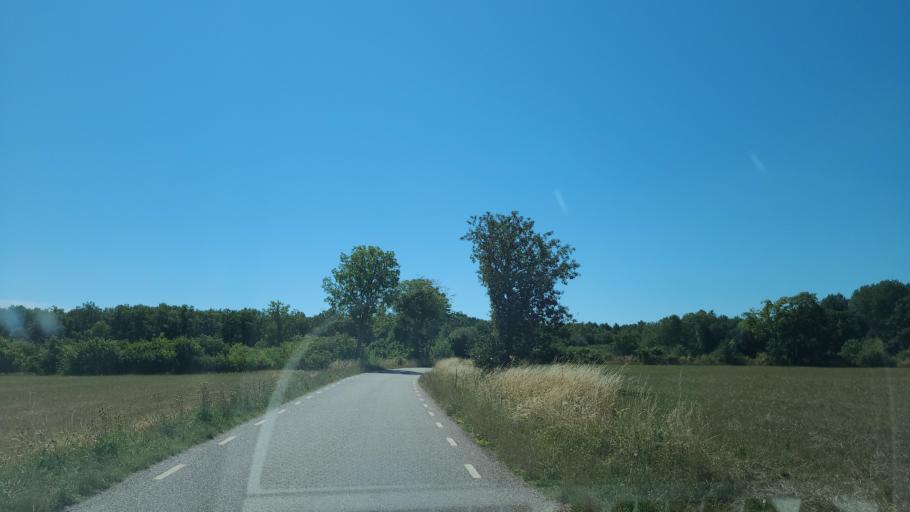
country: SE
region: Kalmar
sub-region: Borgholms Kommun
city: Borgholm
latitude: 56.7583
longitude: 16.6591
